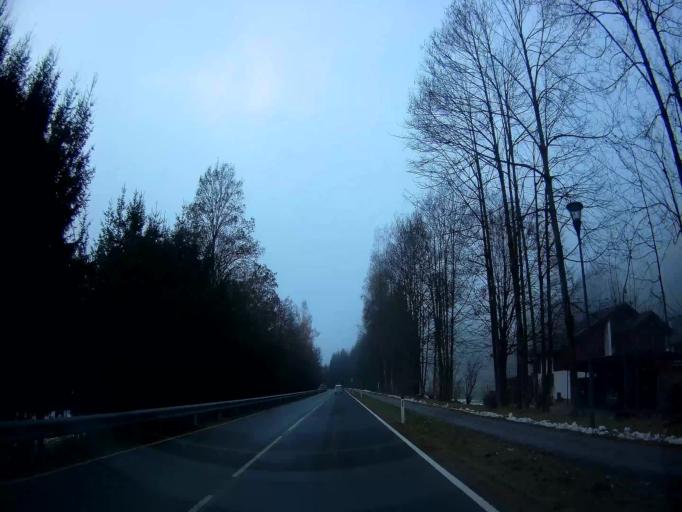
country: AT
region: Salzburg
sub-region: Politischer Bezirk Zell am See
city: Kaprun
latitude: 47.2660
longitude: 12.7478
